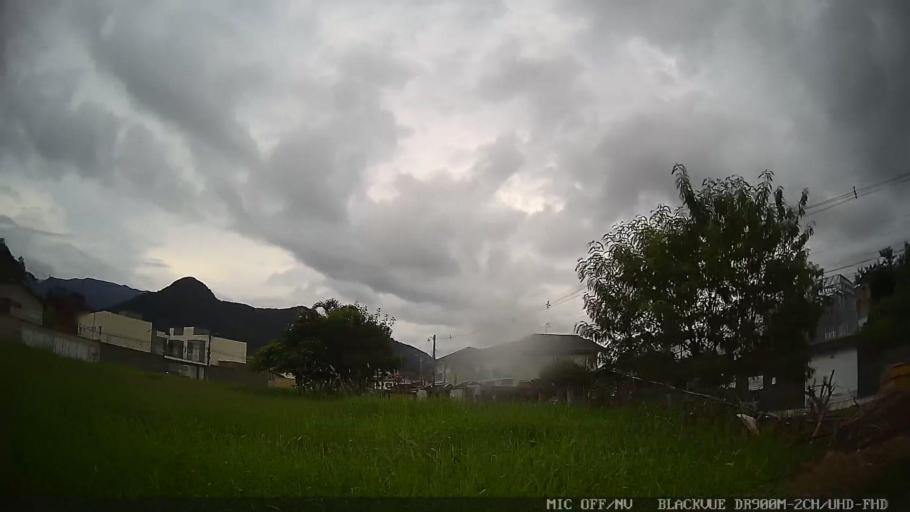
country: BR
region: Sao Paulo
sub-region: Caraguatatuba
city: Caraguatatuba
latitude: -23.6221
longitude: -45.3903
